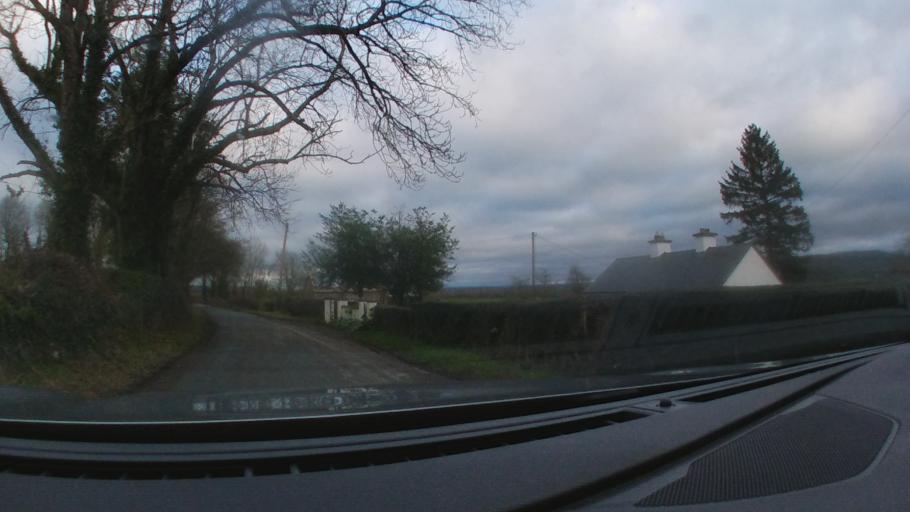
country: IE
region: Leinster
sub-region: Kilkenny
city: Thomastown
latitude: 52.5606
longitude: -7.1366
